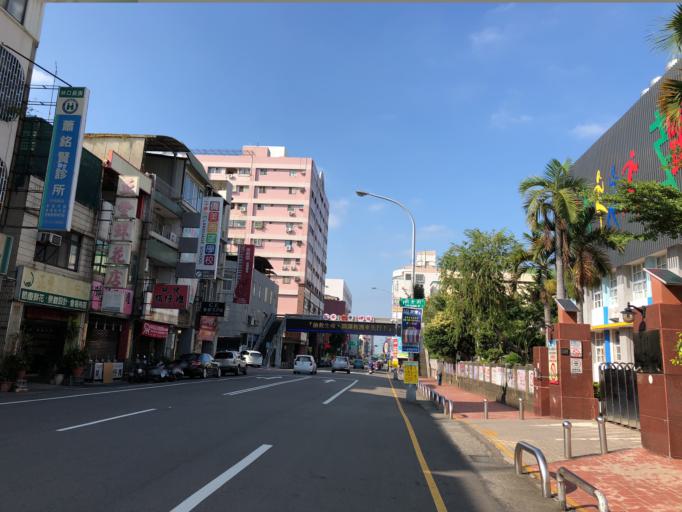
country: TW
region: Taiwan
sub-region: Miaoli
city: Miaoli
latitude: 24.5643
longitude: 120.8242
